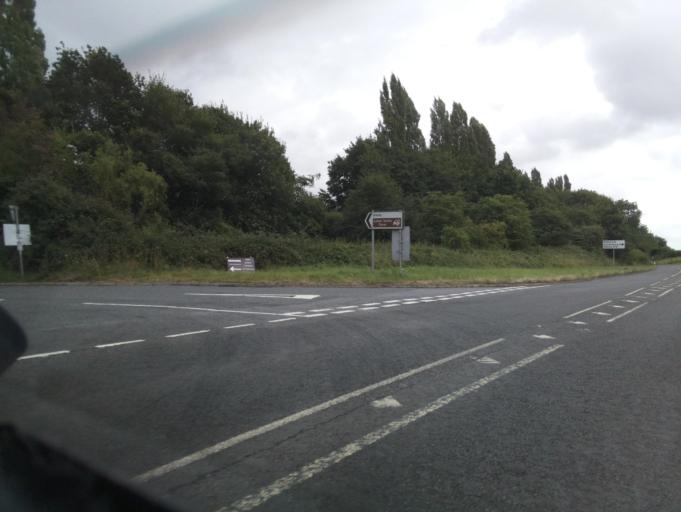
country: GB
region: England
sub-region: Worcestershire
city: Fernhill Heath
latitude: 52.2306
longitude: -2.1701
